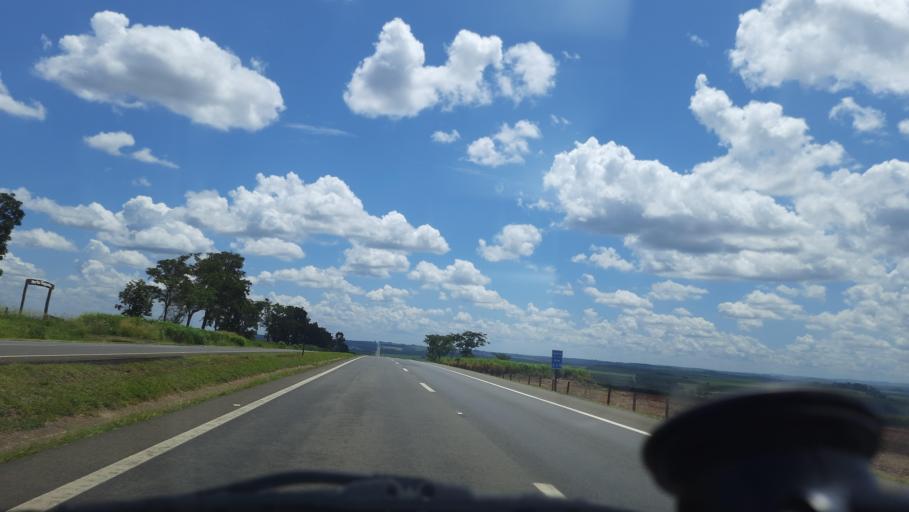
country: BR
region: Sao Paulo
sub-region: Aguai
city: Aguai
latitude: -22.0249
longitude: -47.0338
